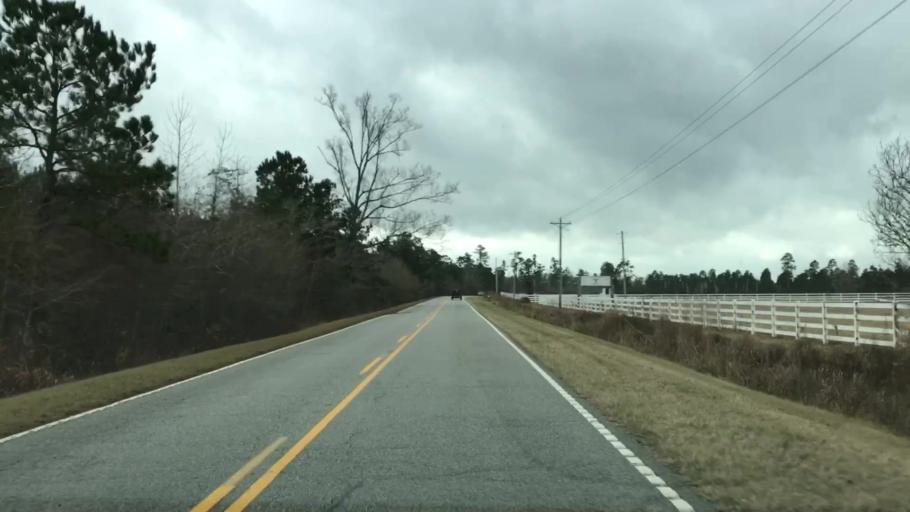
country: US
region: South Carolina
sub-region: Florence County
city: Johnsonville
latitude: 33.6521
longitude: -79.4194
